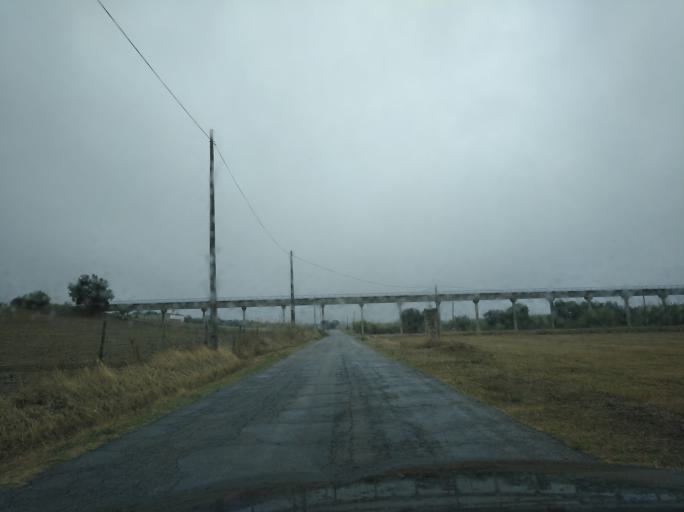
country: PT
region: Portalegre
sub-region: Campo Maior
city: Campo Maior
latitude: 38.9739
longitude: -7.0695
